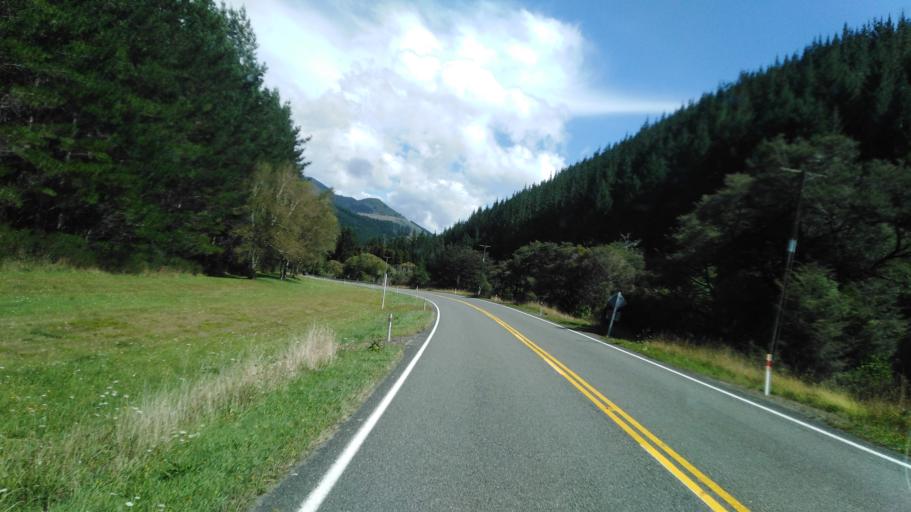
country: NZ
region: Nelson
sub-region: Nelson City
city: Nelson
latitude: -41.1659
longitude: 173.5139
